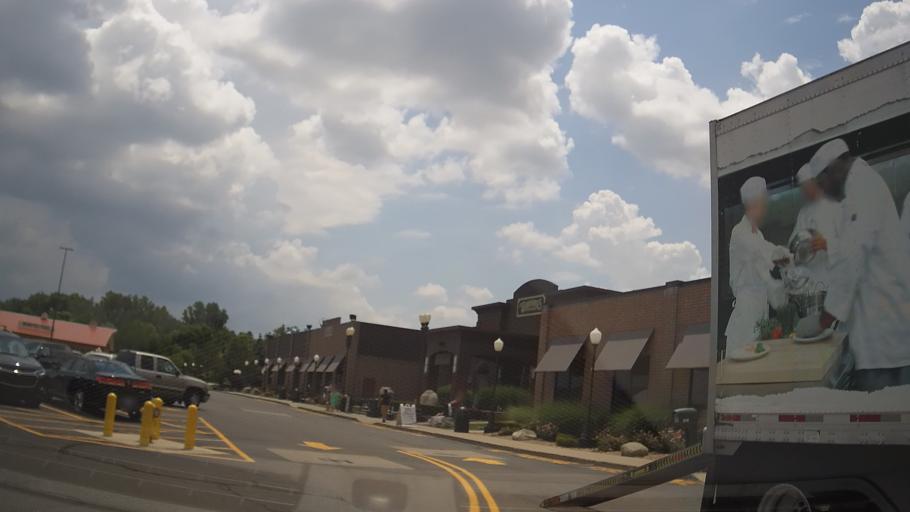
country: US
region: Michigan
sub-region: Macomb County
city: Mount Clemens
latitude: 42.6282
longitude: -82.8953
